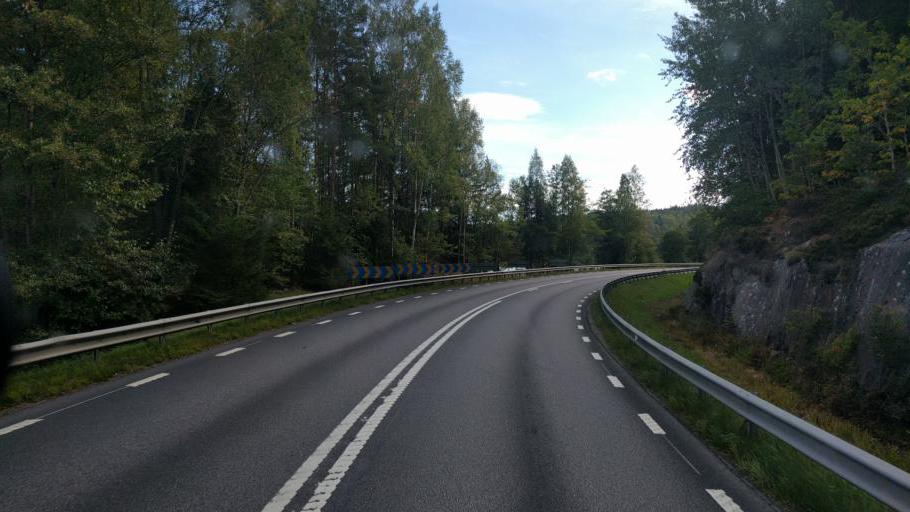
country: SE
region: OEstergoetland
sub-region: Kinda Kommun
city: Kisa
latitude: 57.9594
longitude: 15.6592
